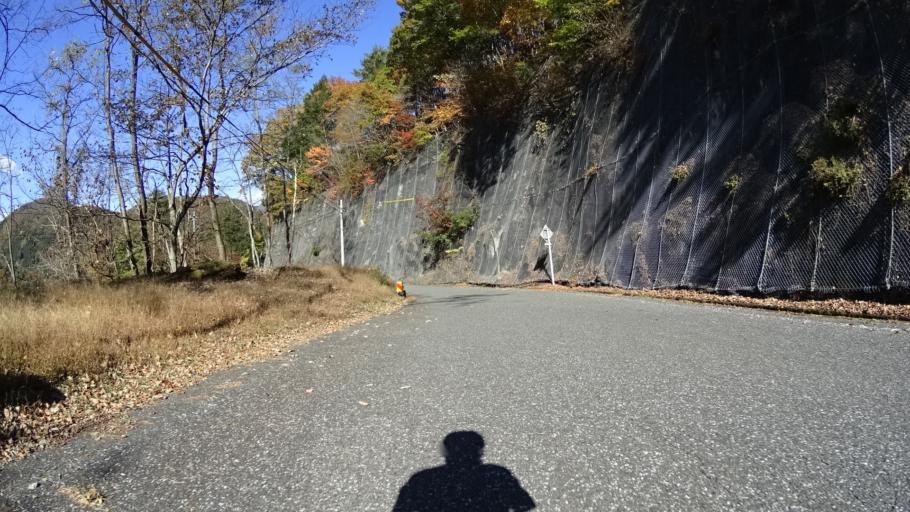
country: JP
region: Yamanashi
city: Otsuki
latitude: 35.7768
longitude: 138.9234
